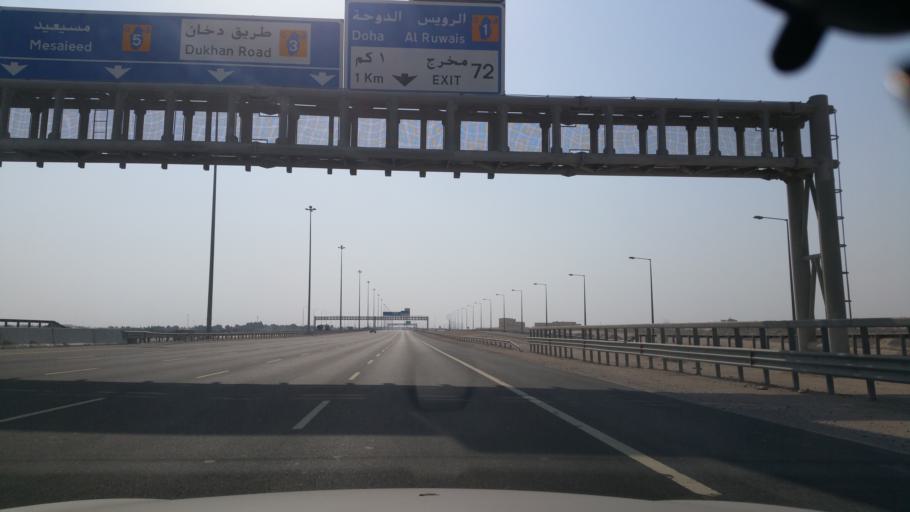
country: QA
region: Baladiyat Umm Salal
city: Umm Salal `Ali
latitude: 25.4543
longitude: 51.4317
